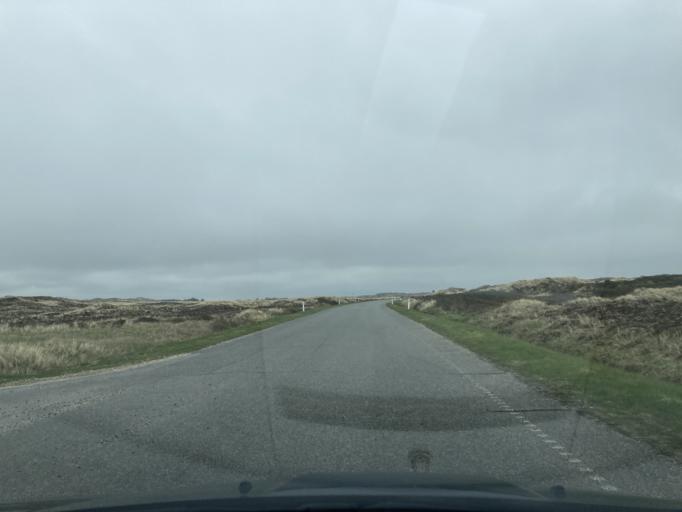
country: DK
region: North Denmark
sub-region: Thisted Kommune
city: Hurup
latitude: 56.9284
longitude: 8.3410
